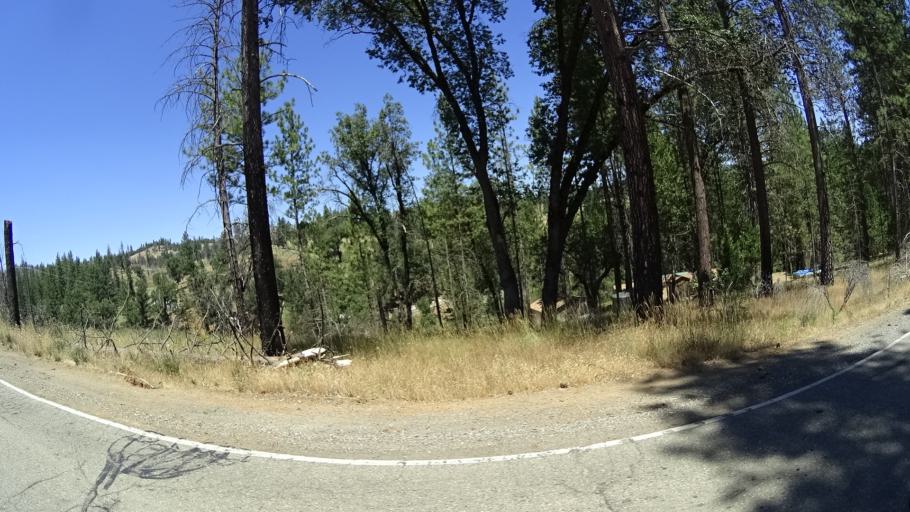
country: US
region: California
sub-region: Calaveras County
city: Mountain Ranch
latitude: 38.2662
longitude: -120.5075
